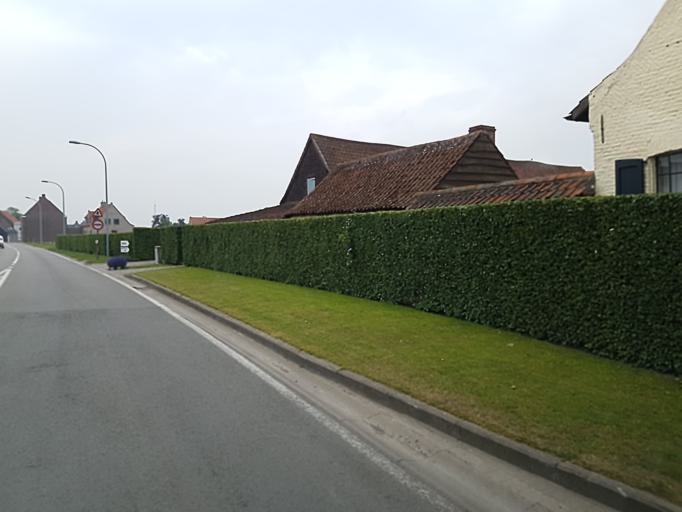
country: BE
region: Flanders
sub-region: Provincie West-Vlaanderen
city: Wielsbeke
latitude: 50.9257
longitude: 3.3920
